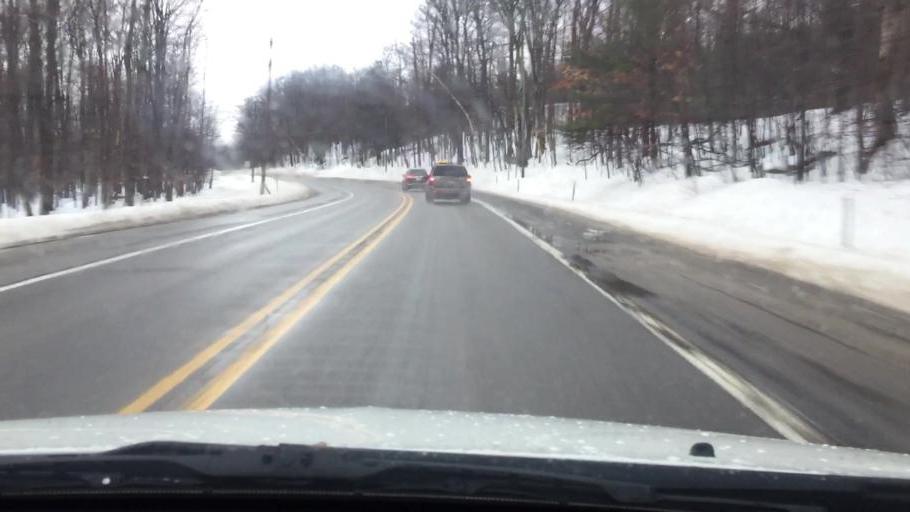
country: US
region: Michigan
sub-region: Charlevoix County
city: East Jordan
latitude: 45.2211
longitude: -85.1756
